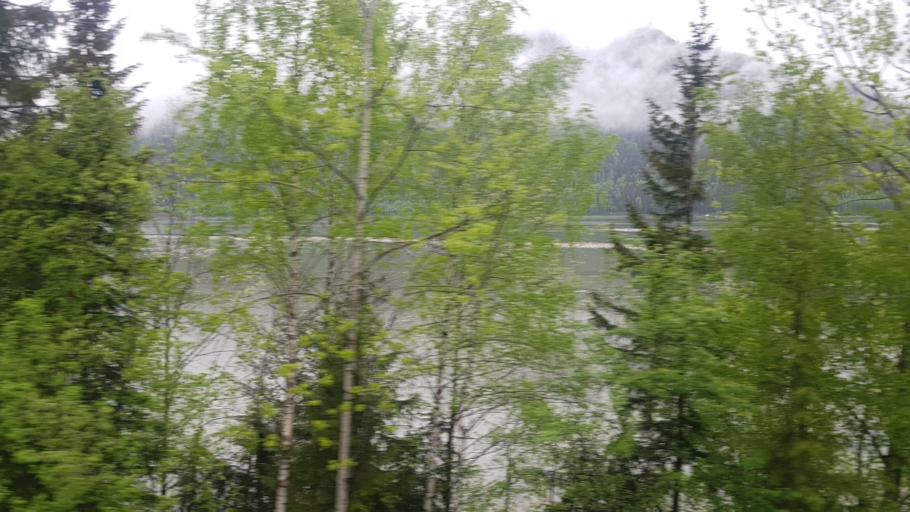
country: NO
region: Oppland
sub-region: Oyer
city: Tretten
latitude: 61.3976
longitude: 10.2350
